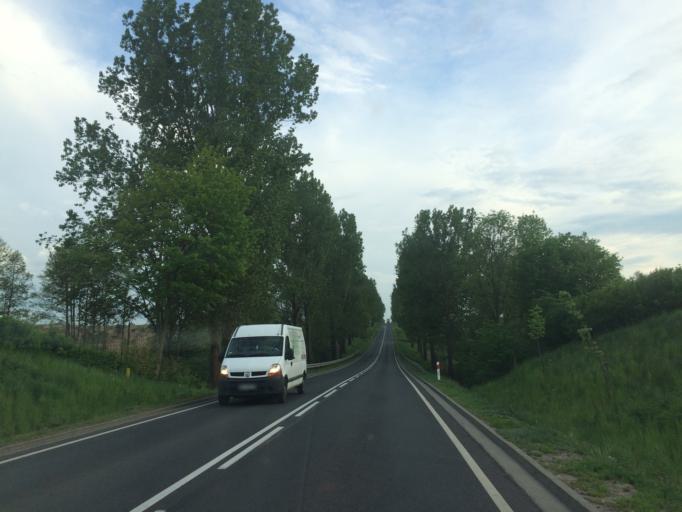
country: PL
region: Warmian-Masurian Voivodeship
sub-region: Powiat nowomiejski
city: Kurzetnik
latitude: 53.3543
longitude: 19.5700
